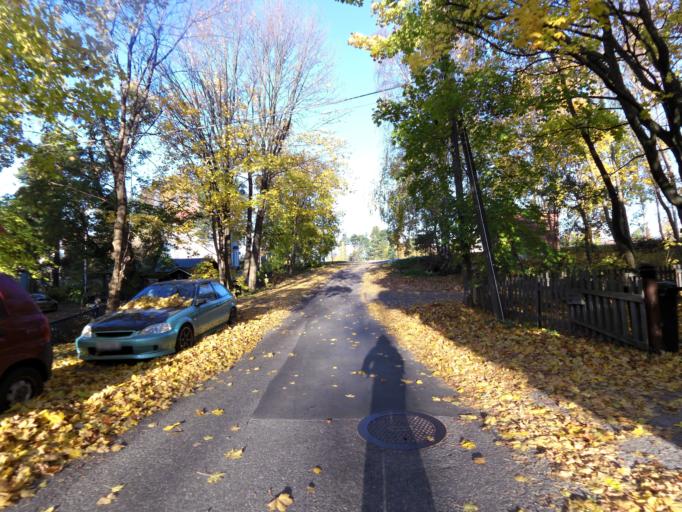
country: FI
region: Uusimaa
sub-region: Helsinki
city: Helsinki
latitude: 60.1851
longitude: 24.9954
